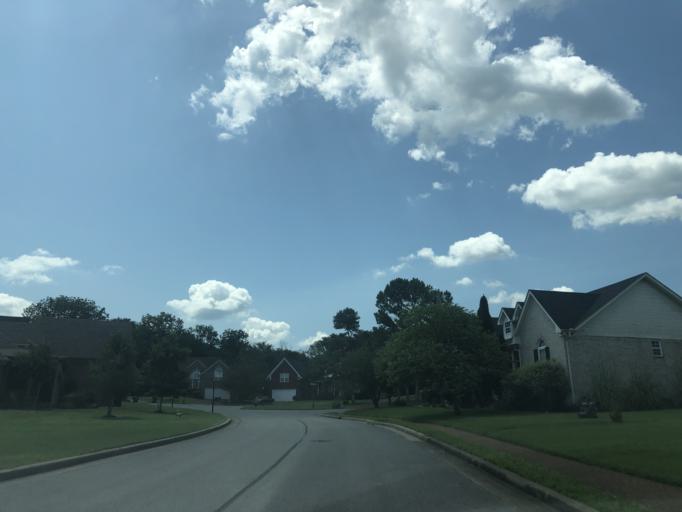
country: US
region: Tennessee
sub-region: Wilson County
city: Green Hill
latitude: 36.1598
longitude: -86.5843
